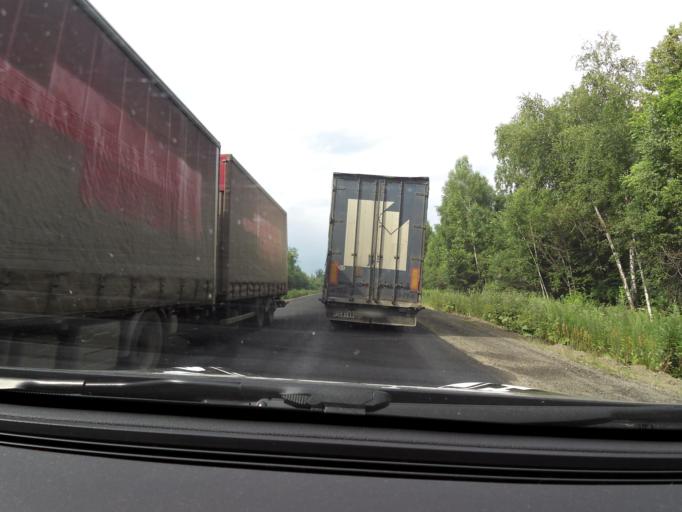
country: RU
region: Chelyabinsk
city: Asha
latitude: 54.8652
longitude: 57.1688
